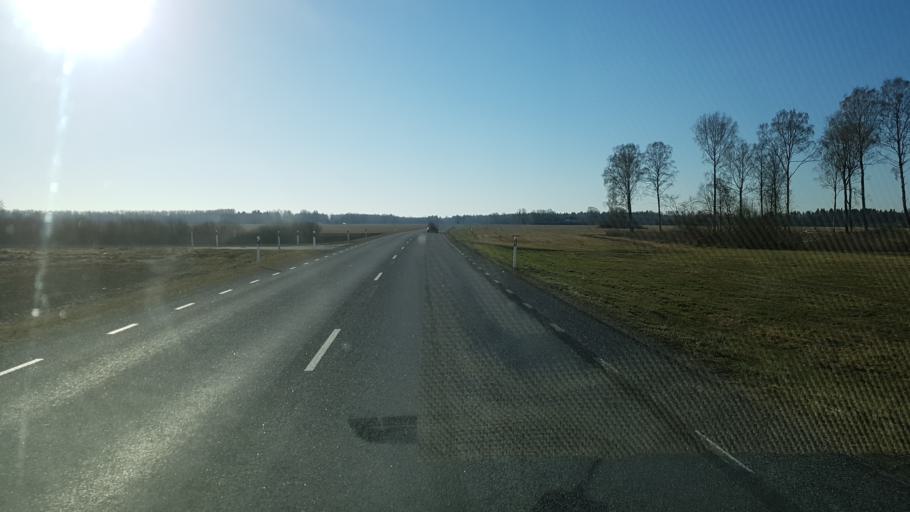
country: EE
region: Jaervamaa
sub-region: Tueri vald
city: Sarevere
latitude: 58.7751
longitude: 25.5103
